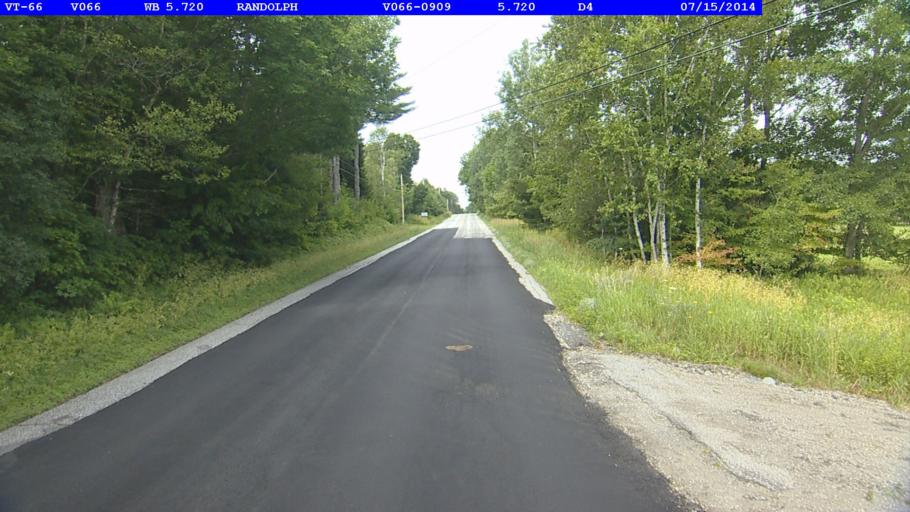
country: US
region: Vermont
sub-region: Orange County
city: Randolph
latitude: 43.9587
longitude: -72.5770
